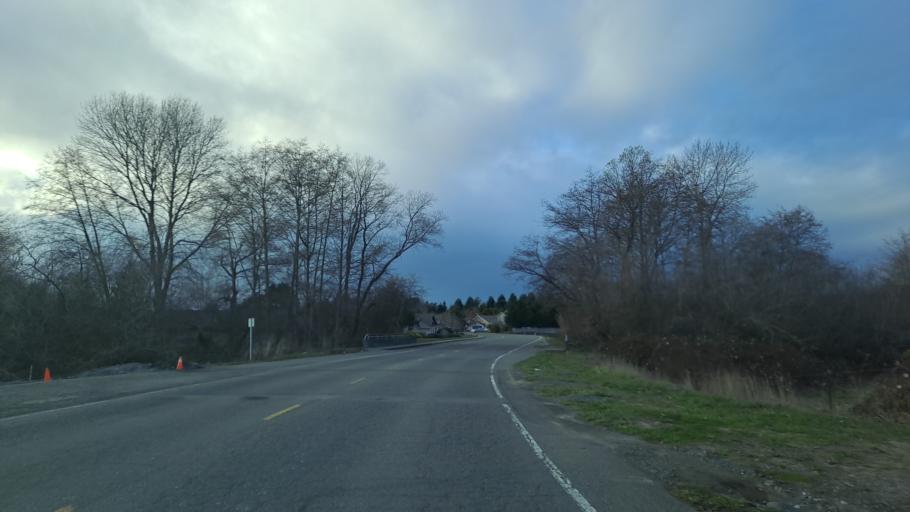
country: US
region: California
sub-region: Humboldt County
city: Fortuna
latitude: 40.5834
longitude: -124.1372
